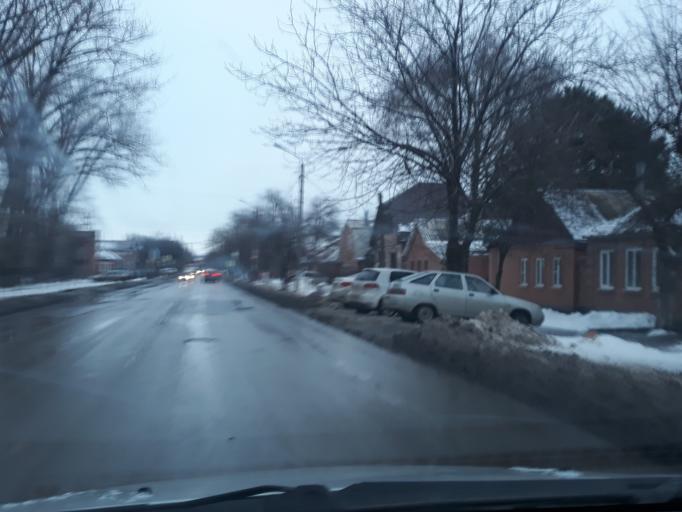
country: RU
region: Rostov
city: Taganrog
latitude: 47.2374
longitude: 38.8768
